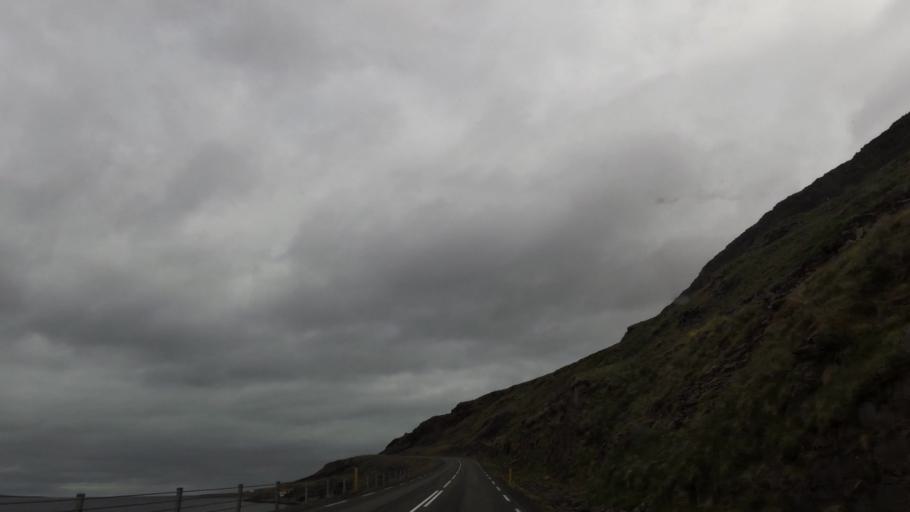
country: IS
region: Westfjords
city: Isafjoerdur
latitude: 65.9939
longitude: -22.7788
